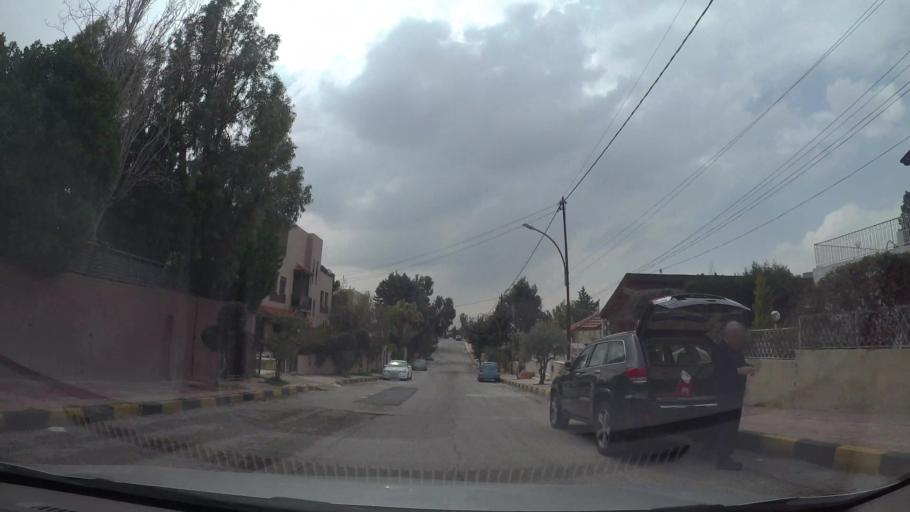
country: JO
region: Amman
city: Umm as Summaq
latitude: 31.8949
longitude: 35.8584
